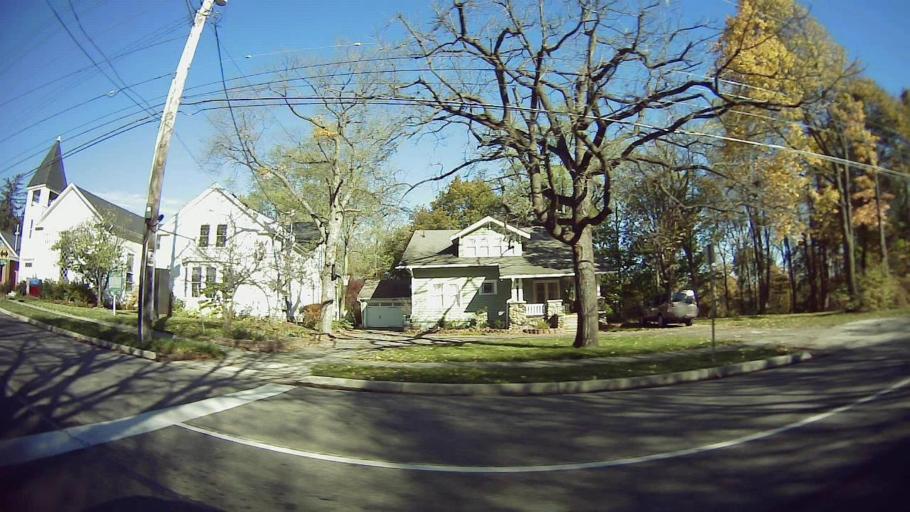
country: US
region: Michigan
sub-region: Oakland County
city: Farmington
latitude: 42.4668
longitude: -83.3760
